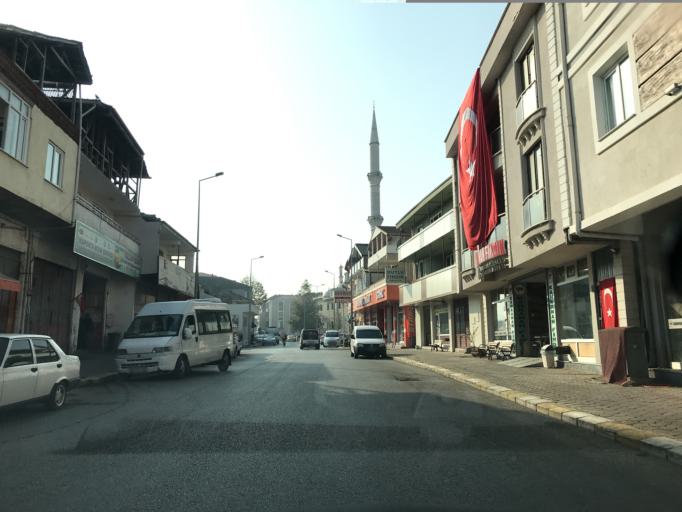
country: TR
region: Duzce
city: Cumayeri
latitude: 40.8778
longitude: 30.9502
